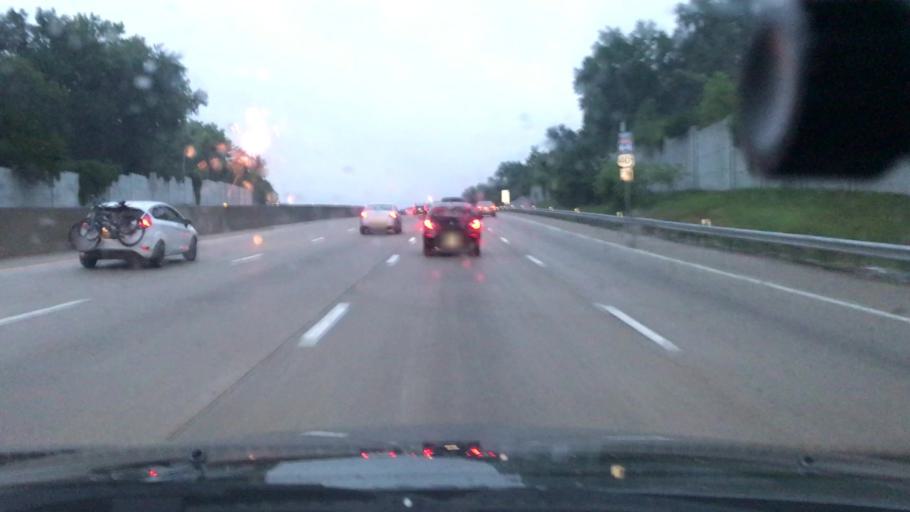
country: US
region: Missouri
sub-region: Saint Louis County
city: Ladue
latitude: 38.6307
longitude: -90.3695
